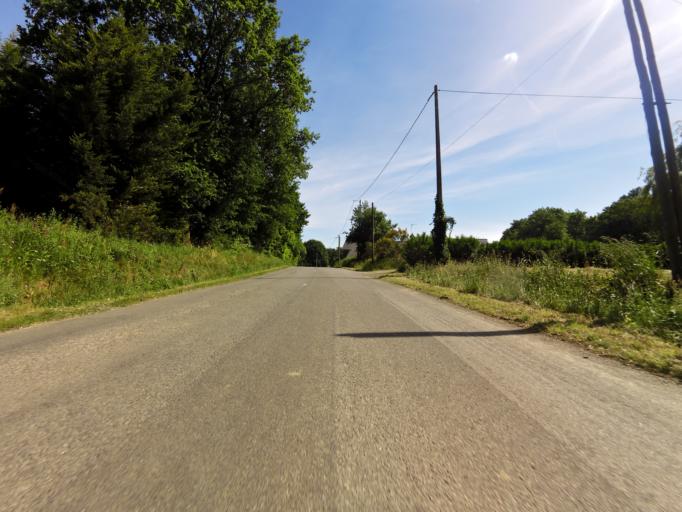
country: FR
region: Brittany
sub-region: Departement du Morbihan
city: Malansac
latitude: 47.6912
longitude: -2.3058
